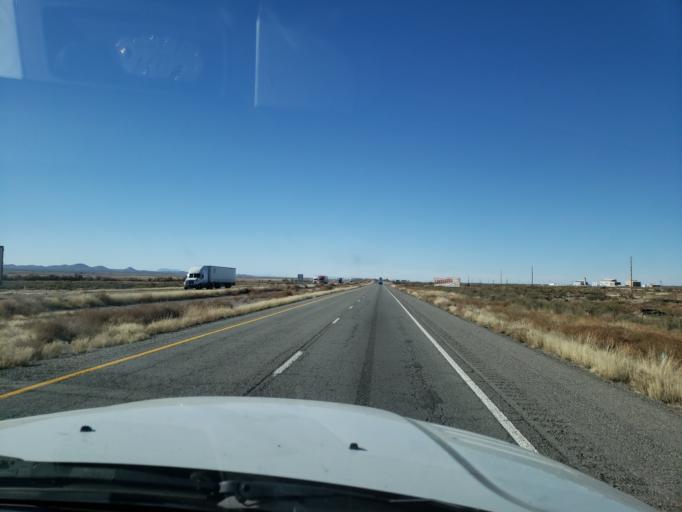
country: US
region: New Mexico
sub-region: Hidalgo County
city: Lordsburg
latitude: 32.3080
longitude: -108.5997
